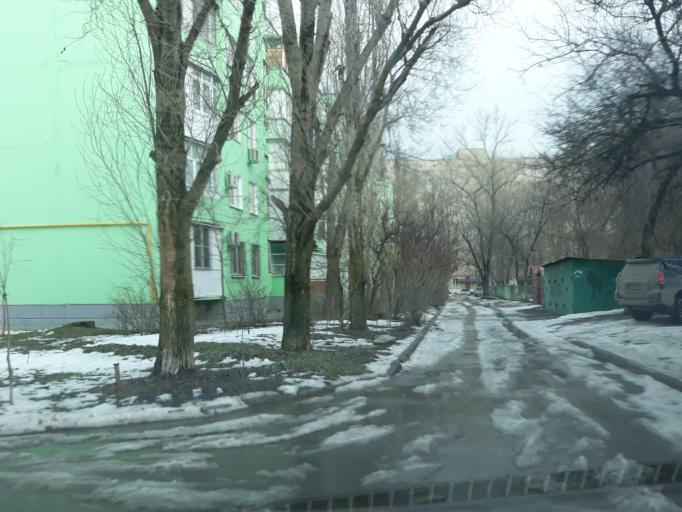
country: RU
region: Rostov
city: Taganrog
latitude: 47.2525
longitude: 38.9139
